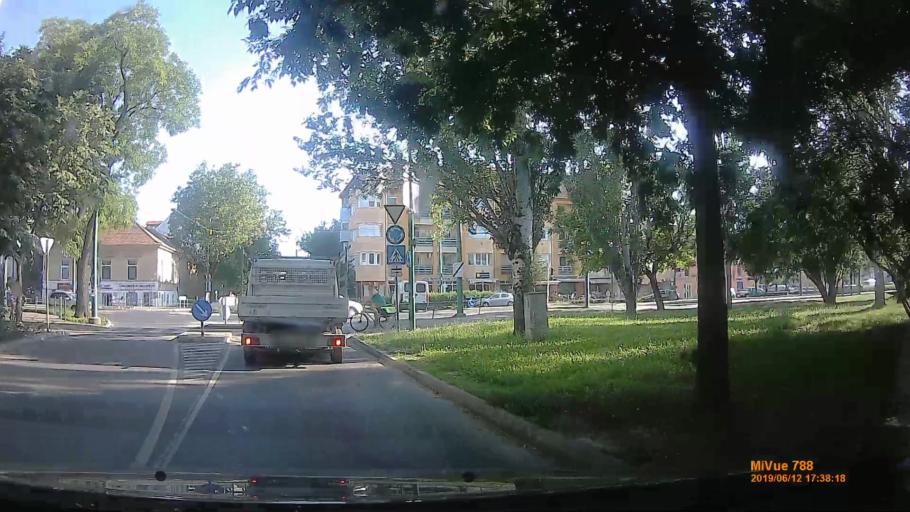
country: HU
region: Csongrad
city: Szeged
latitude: 46.2530
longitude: 20.1348
